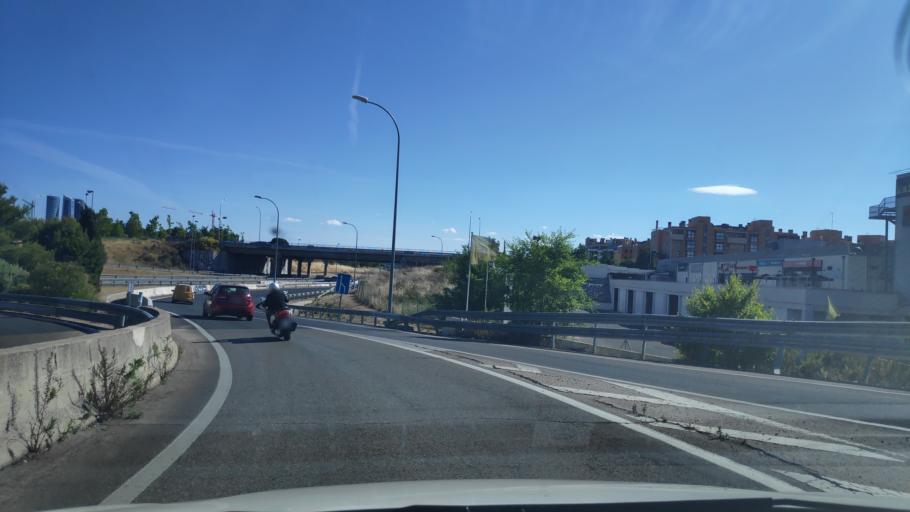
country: ES
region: Madrid
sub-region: Provincia de Madrid
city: Las Tablas
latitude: 40.5108
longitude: -3.6889
